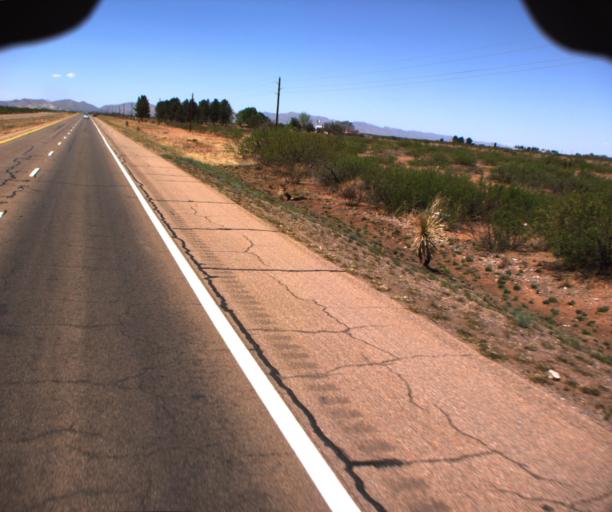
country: US
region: Arizona
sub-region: Cochise County
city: Pirtleville
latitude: 31.3562
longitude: -109.6212
